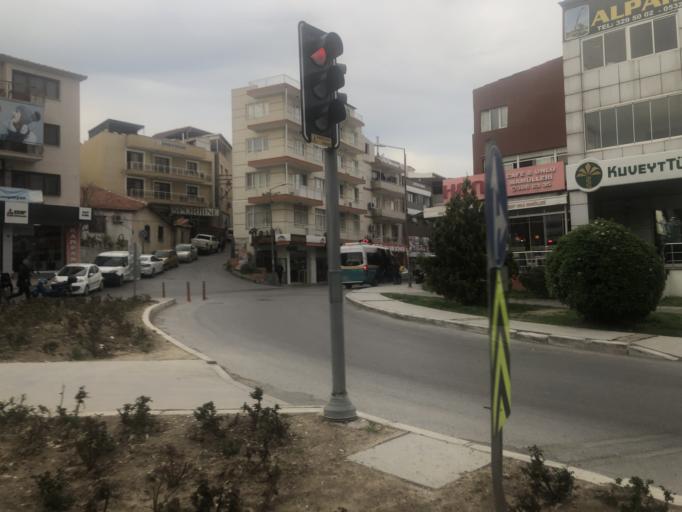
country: TR
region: Izmir
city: Karsiyaka
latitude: 38.4905
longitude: 27.0680
